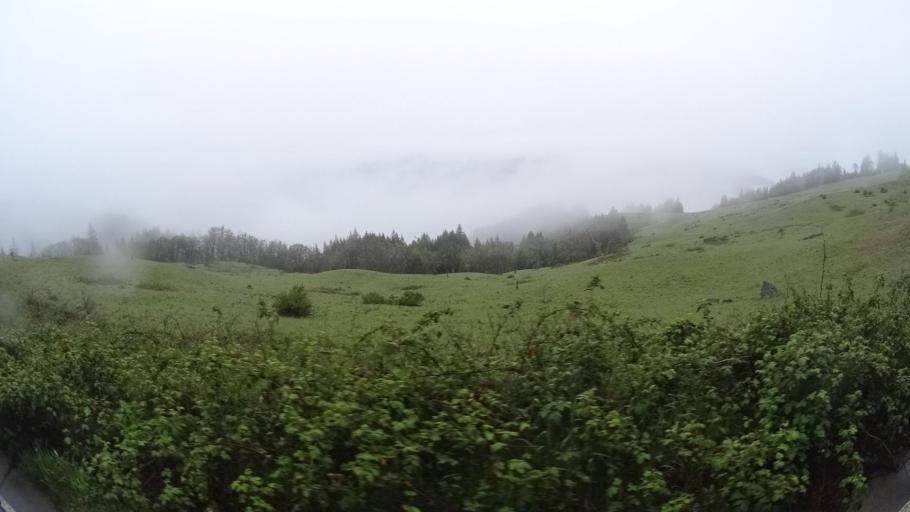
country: US
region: California
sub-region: Humboldt County
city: Westhaven-Moonstone
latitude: 41.1883
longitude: -123.9300
